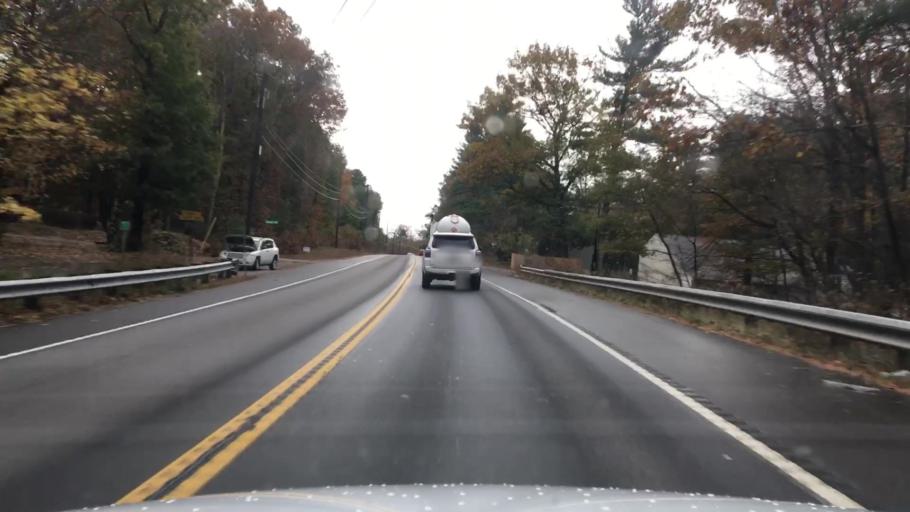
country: US
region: New Hampshire
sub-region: Strafford County
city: Lee
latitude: 43.1342
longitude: -71.0203
